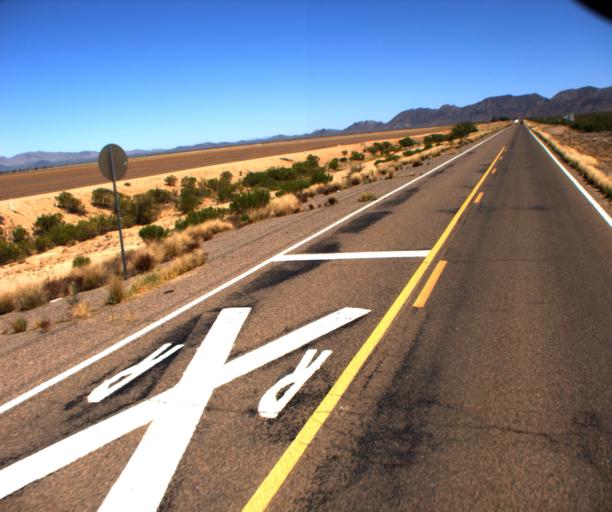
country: US
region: Arizona
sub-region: Yavapai County
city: Congress
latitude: 33.9518
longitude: -113.1416
